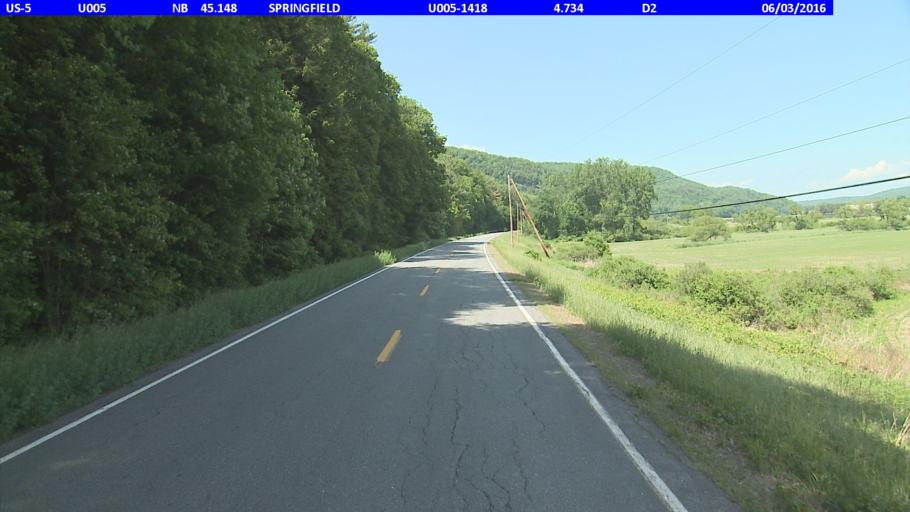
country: US
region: New Hampshire
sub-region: Sullivan County
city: Charlestown
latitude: 43.2819
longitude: -72.4138
